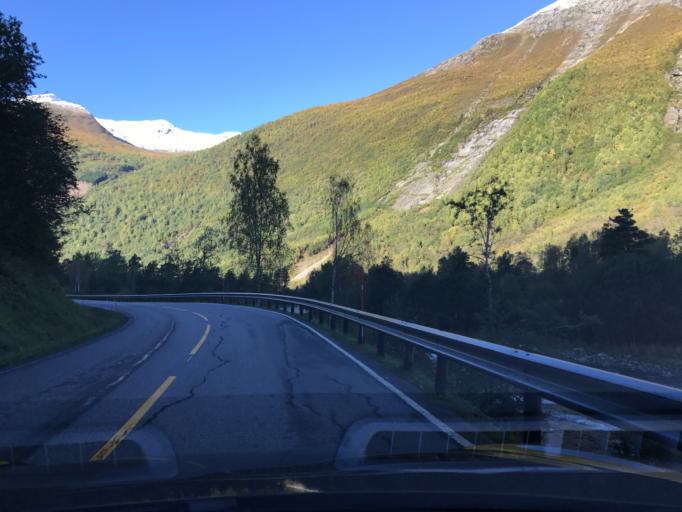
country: NO
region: More og Romsdal
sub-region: Norddal
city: Valldal
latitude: 62.3135
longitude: 7.2819
